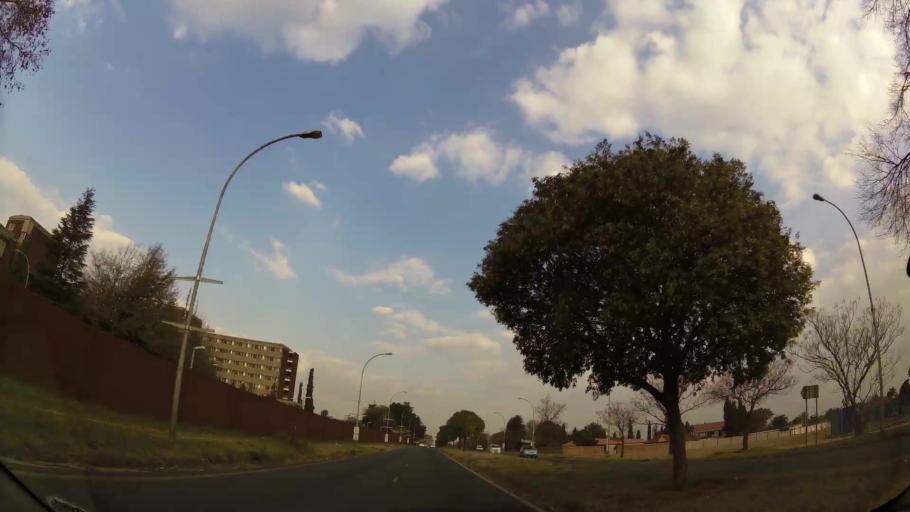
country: ZA
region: Gauteng
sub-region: Ekurhuleni Metropolitan Municipality
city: Benoni
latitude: -26.1595
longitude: 28.3050
